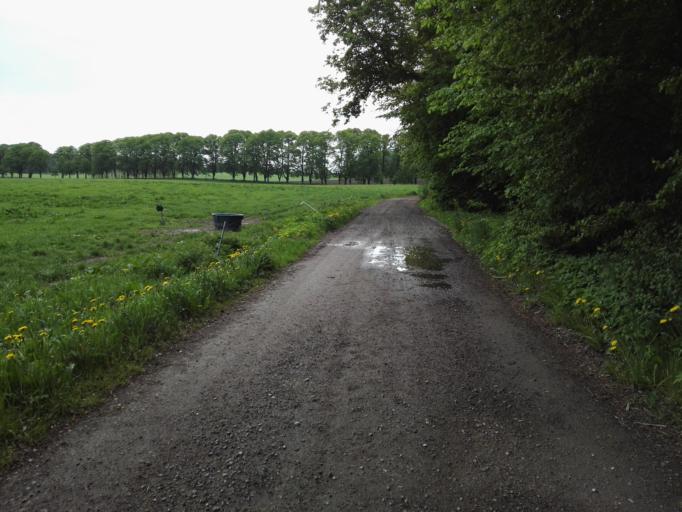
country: DK
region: Capital Region
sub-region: Frederikssund Kommune
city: Skibby
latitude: 55.7864
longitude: 11.9399
